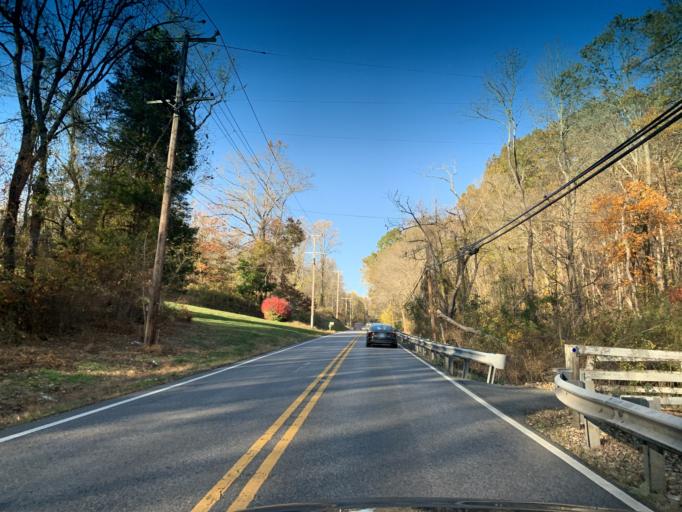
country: US
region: Maryland
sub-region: Harford County
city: Jarrettsville
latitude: 39.5595
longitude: -76.4622
